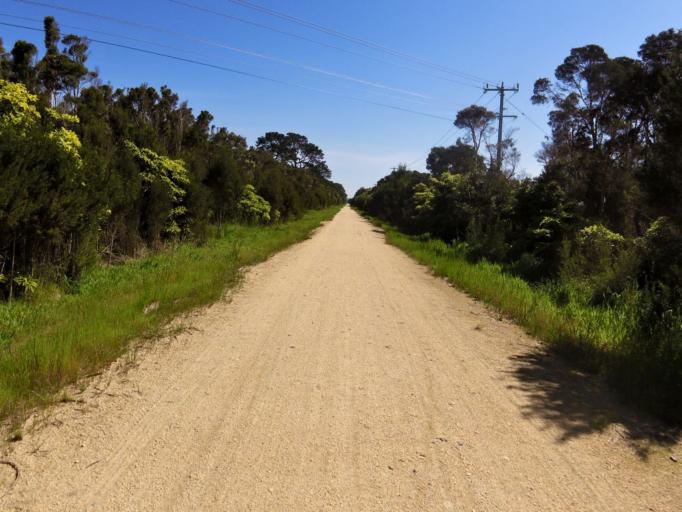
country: AU
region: Victoria
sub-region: Latrobe
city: Morwell
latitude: -38.6657
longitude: 146.3064
